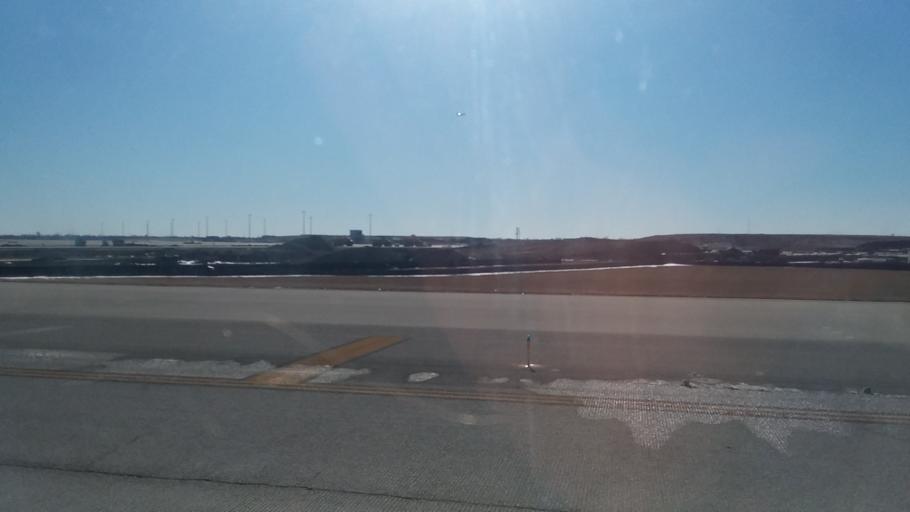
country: US
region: Illinois
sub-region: DuPage County
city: Bensenville
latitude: 41.9848
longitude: -87.9265
